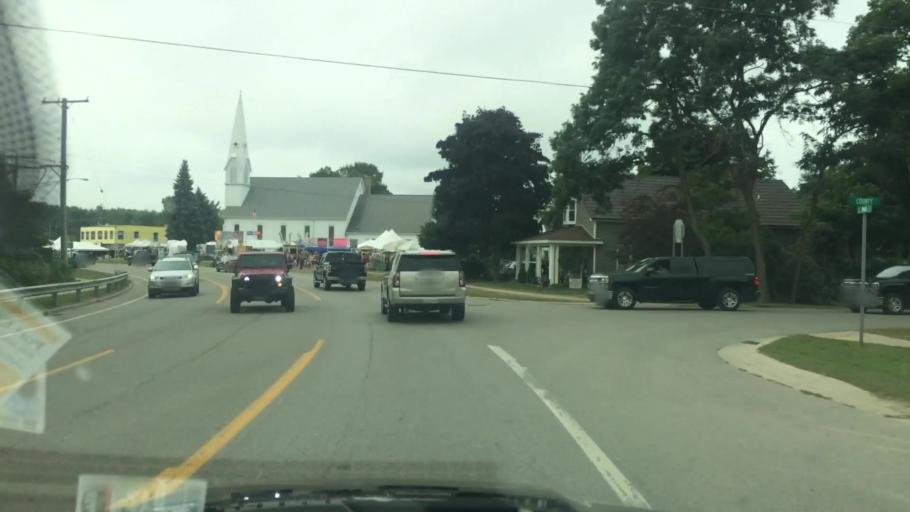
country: US
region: Michigan
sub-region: Huron County
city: Pigeon
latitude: 43.9458
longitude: -83.2729
